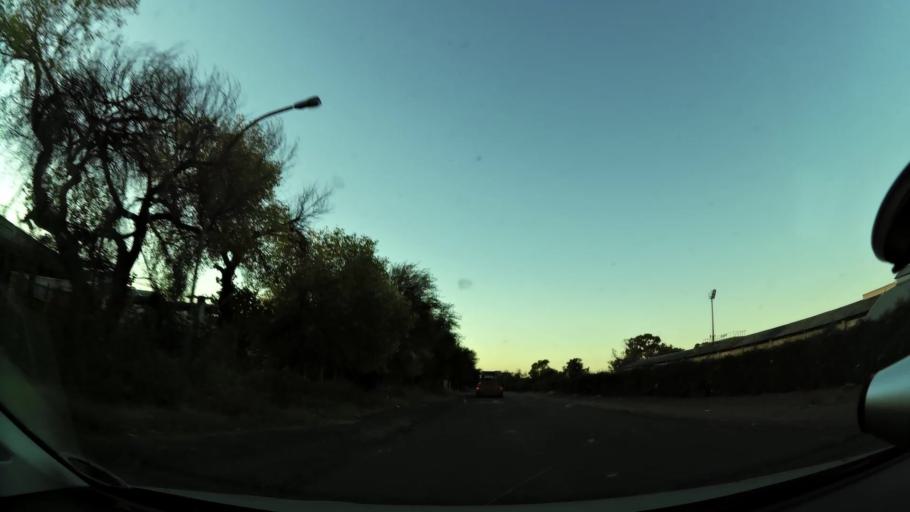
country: ZA
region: Northern Cape
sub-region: Frances Baard District Municipality
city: Kimberley
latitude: -28.7270
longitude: 24.7754
